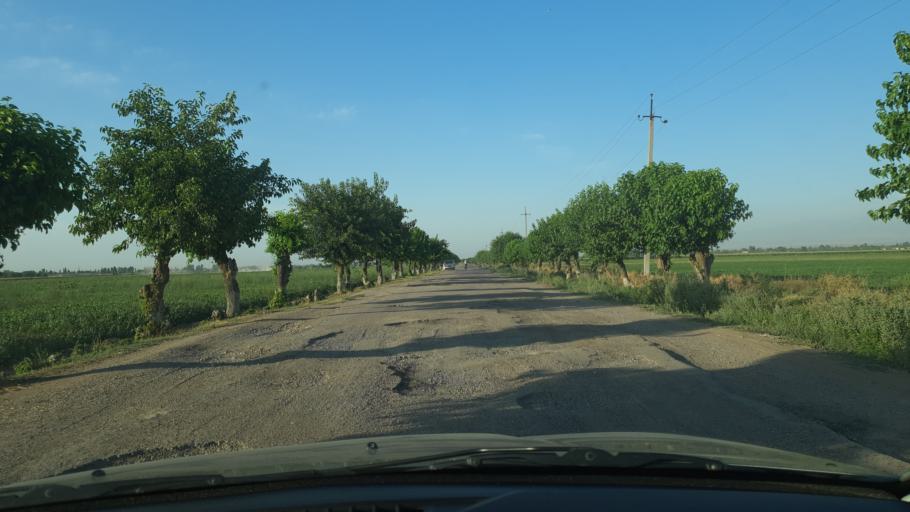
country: UZ
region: Toshkent
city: Tuytepa
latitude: 41.0922
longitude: 69.3695
